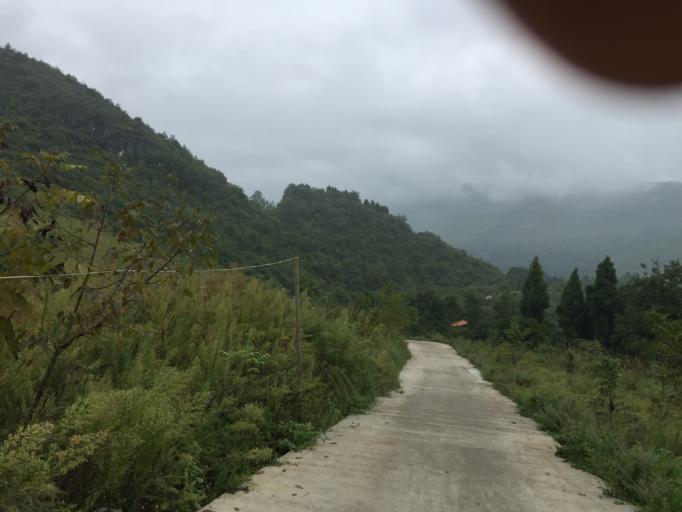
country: CN
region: Guizhou Sheng
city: Changfeng
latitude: 28.4263
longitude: 108.1350
